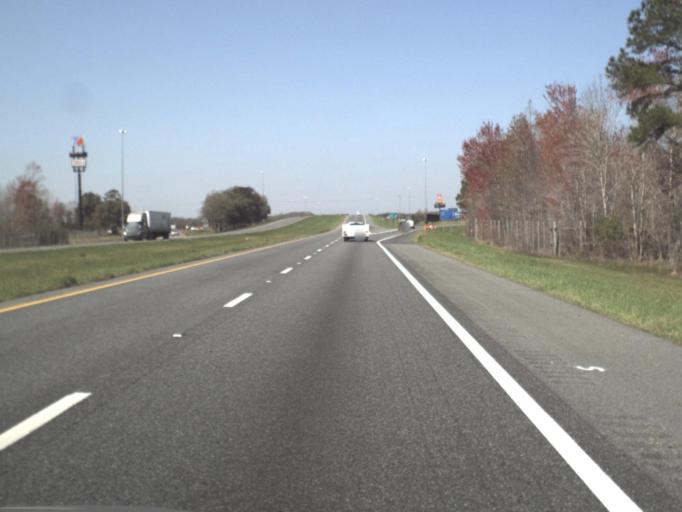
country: US
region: Florida
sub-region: Jackson County
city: Marianna
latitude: 30.7202
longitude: -85.1791
